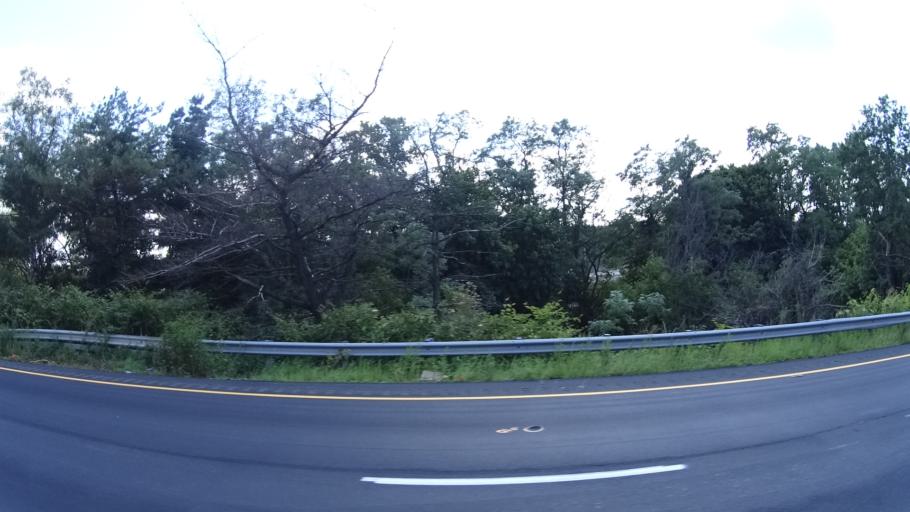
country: US
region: New Jersey
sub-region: Union County
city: Springfield
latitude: 40.7153
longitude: -74.2967
